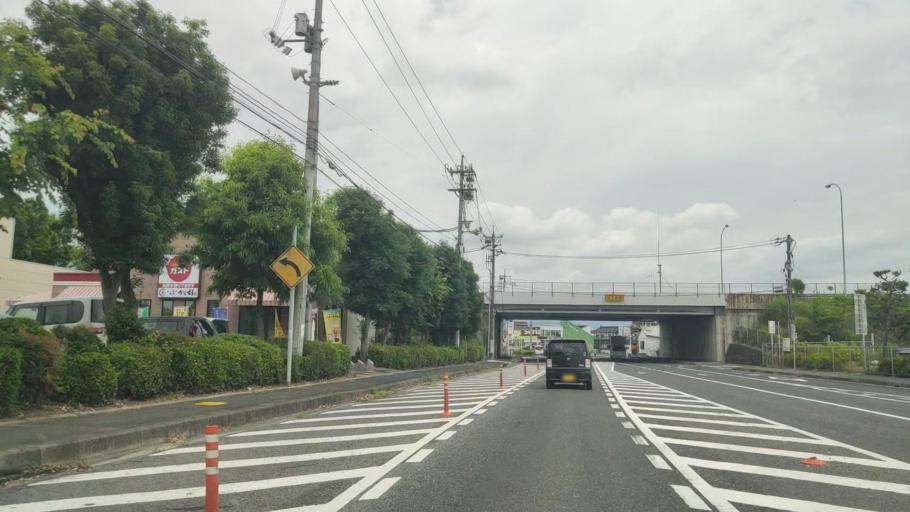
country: JP
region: Okayama
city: Tsuyama
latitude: 35.0640
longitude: 134.0488
